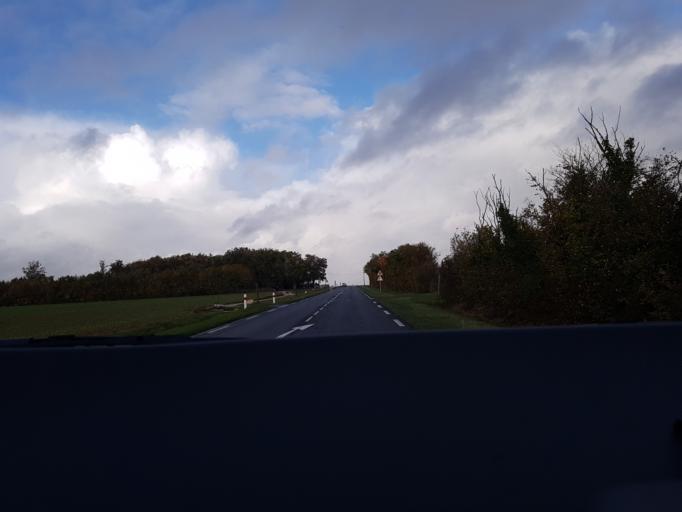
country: FR
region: Poitou-Charentes
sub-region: Departement de la Charente-Maritime
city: Aulnay
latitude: 46.0520
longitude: -0.3333
